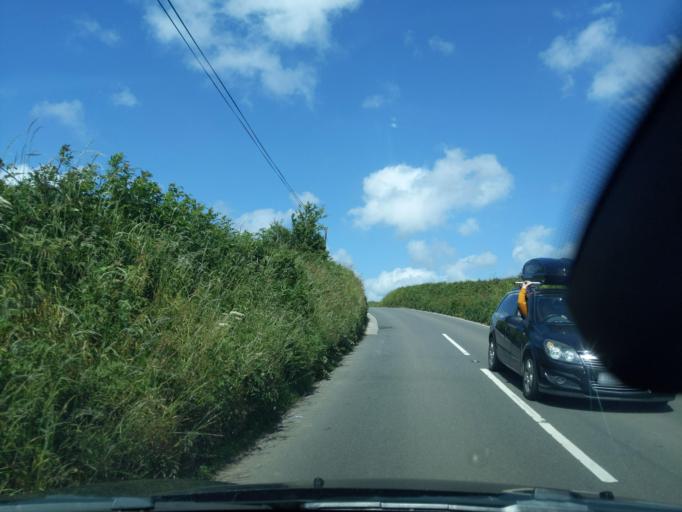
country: GB
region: England
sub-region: Devon
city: Great Torrington
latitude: 50.9661
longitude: -4.1161
